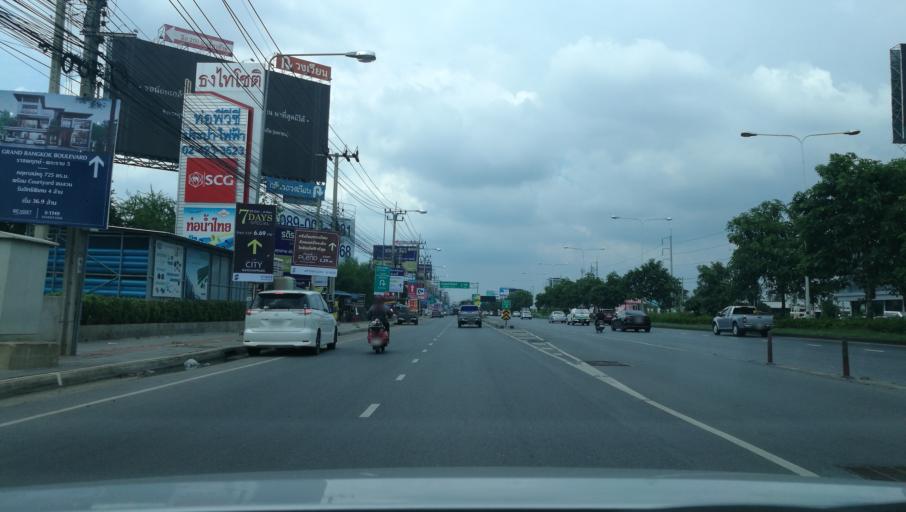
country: TH
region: Nonthaburi
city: Bang Kruai
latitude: 13.8125
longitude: 100.4493
